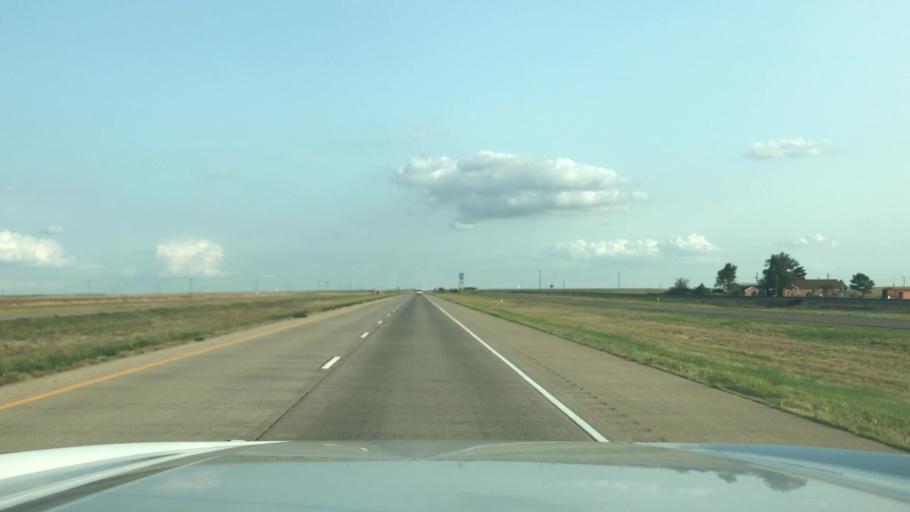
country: US
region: Texas
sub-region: Swisher County
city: Tulia
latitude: 34.6218
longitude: -101.8149
